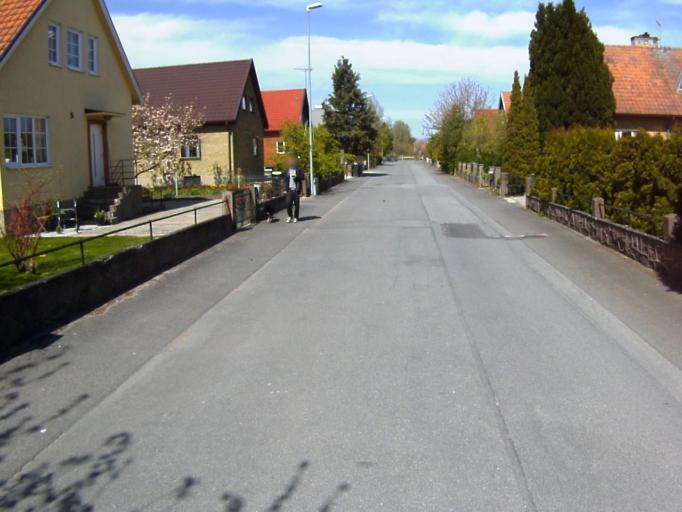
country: SE
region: Skane
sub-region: Kristianstads Kommun
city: Kristianstad
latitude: 56.0522
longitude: 14.1549
